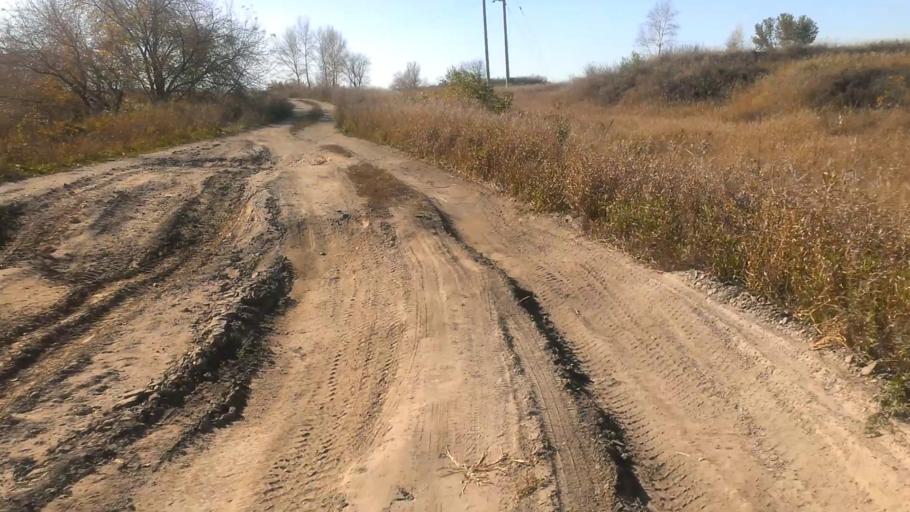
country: RU
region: Altai Krai
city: Novoaltaysk
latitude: 53.3680
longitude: 83.9474
